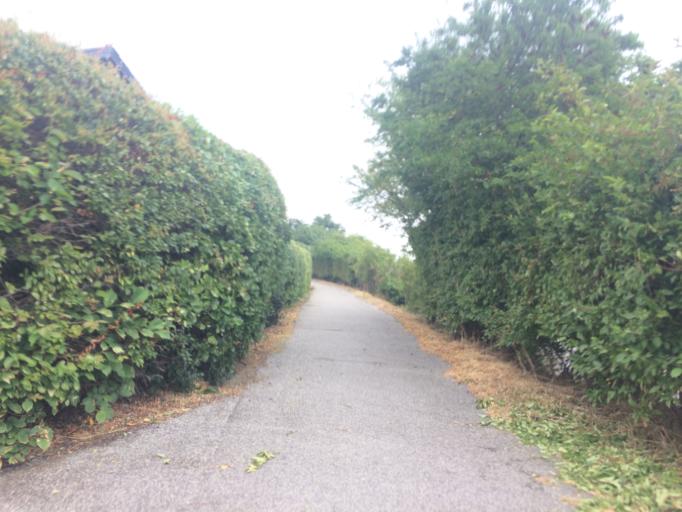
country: DK
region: Central Jutland
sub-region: Struer Kommune
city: Struer
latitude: 56.4883
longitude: 8.6100
